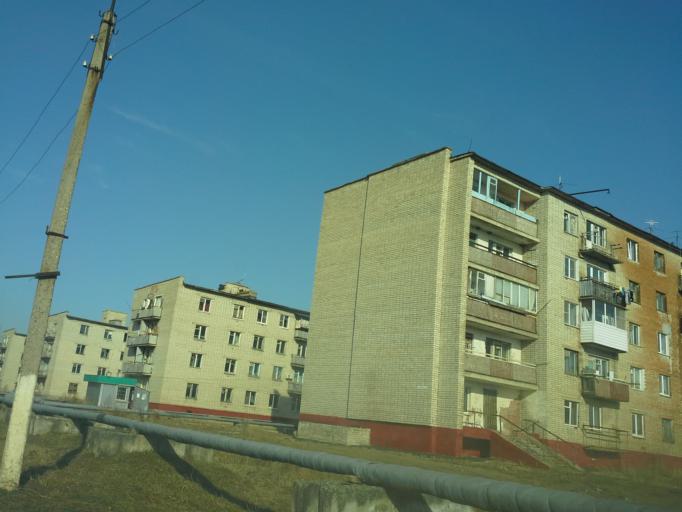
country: RU
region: Jewish Autonomous Oblast
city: Priamurskiy
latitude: 48.3594
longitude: 134.7963
